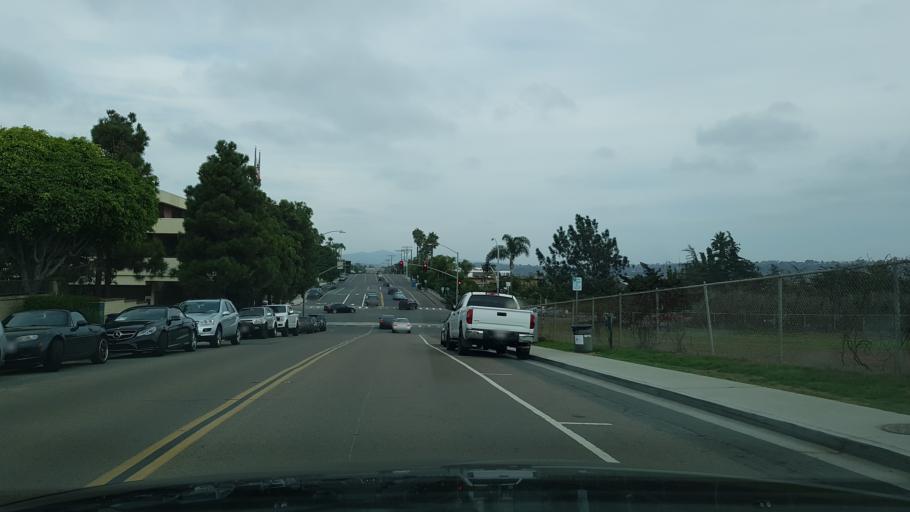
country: US
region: California
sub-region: San Diego County
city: Solana Beach
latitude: 32.9803
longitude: -117.2703
